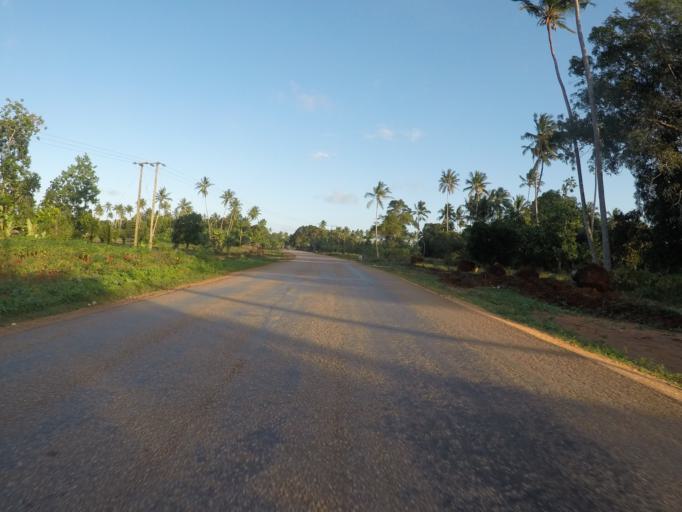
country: TZ
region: Zanzibar North
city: Gamba
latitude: -5.8919
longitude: 39.2896
